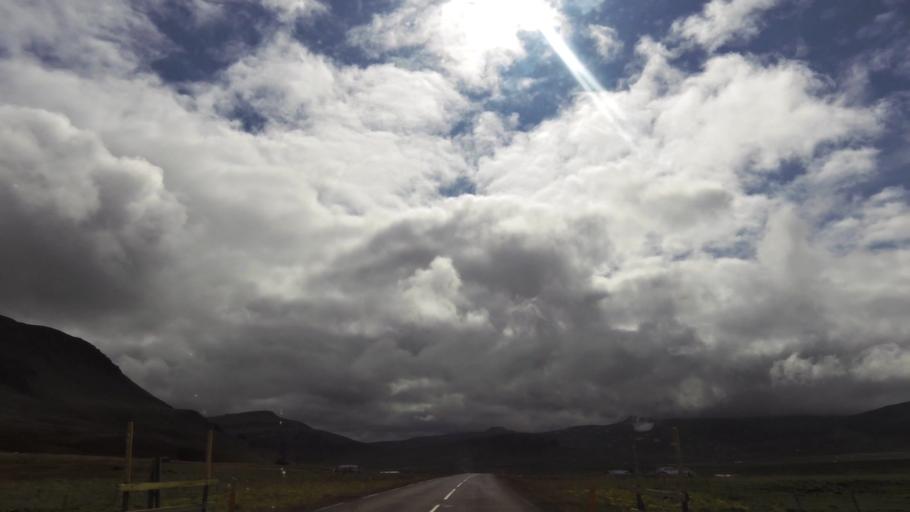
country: IS
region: West
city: Borgarnes
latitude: 65.3994
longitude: -21.8809
